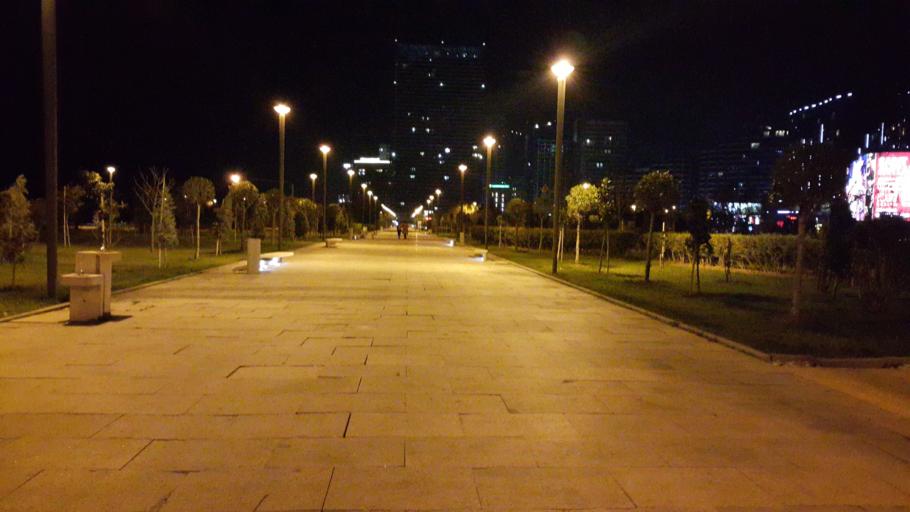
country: GE
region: Ajaria
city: Batumi
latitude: 41.6265
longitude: 41.5976
